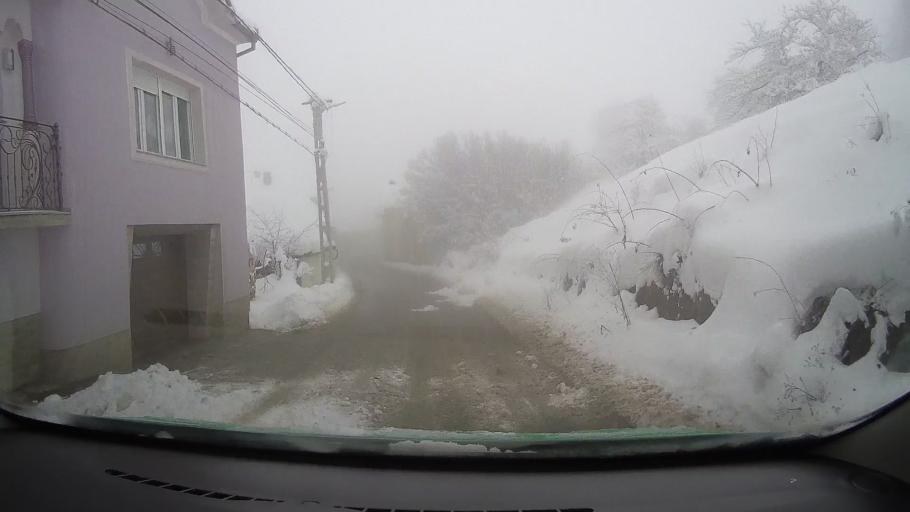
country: RO
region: Sibiu
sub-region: Comuna Poiana Sibiului
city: Poiana Sibiului
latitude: 45.8083
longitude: 23.7381
